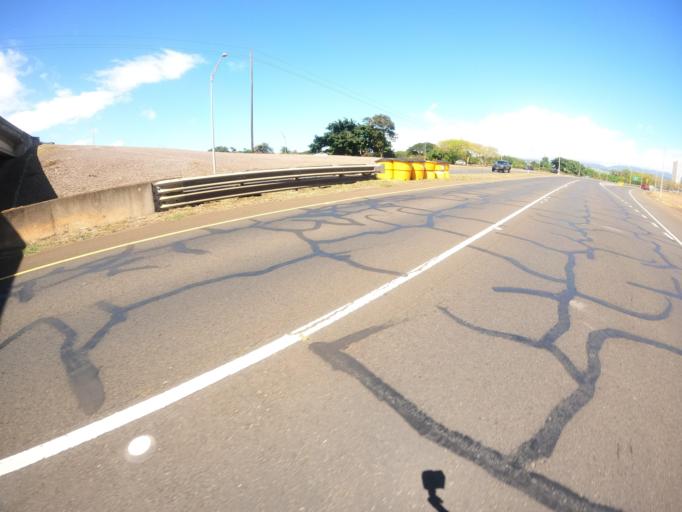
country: US
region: Hawaii
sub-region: Honolulu County
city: Pearl City, Manana
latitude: 21.3933
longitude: -157.9875
